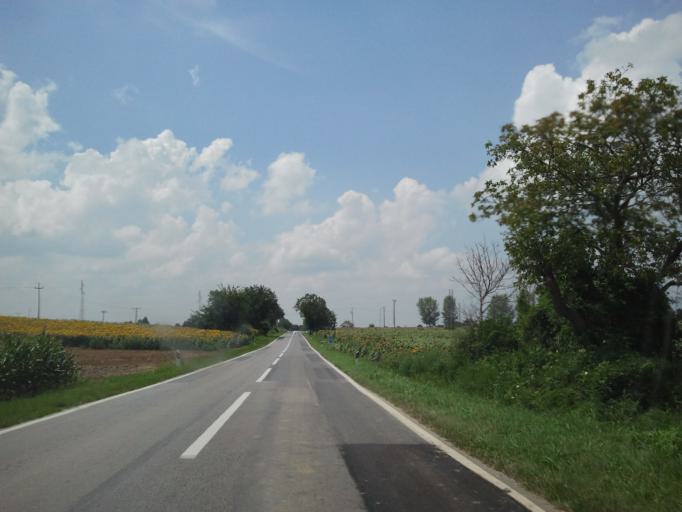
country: HR
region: Vukovarsko-Srijemska
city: Lovas
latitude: 45.2567
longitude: 19.1847
